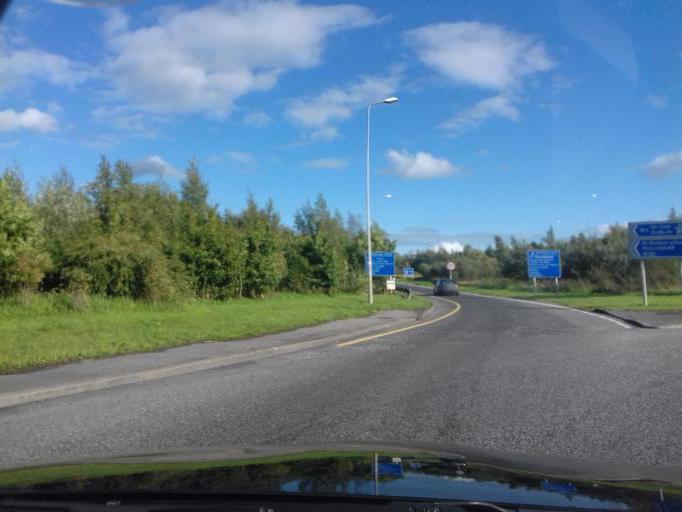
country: IE
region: Leinster
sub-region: An Iarmhi
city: Kilbeggan
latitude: 53.3593
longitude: -7.4950
